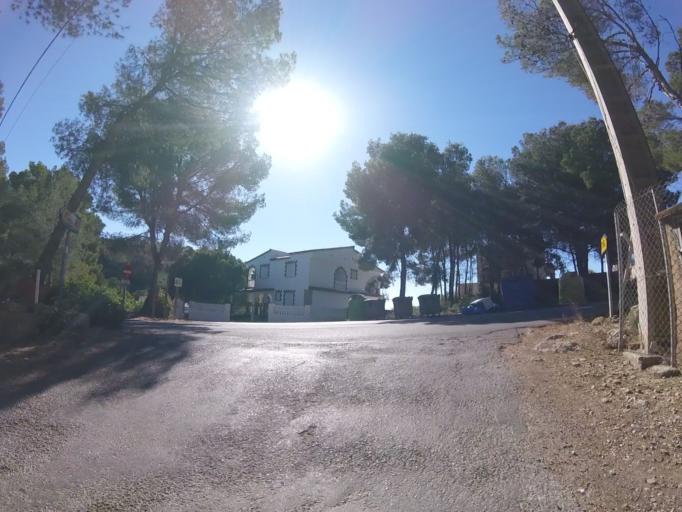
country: ES
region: Valencia
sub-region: Provincia de Castello
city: Orpesa/Oropesa del Mar
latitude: 40.0745
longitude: 0.1183
